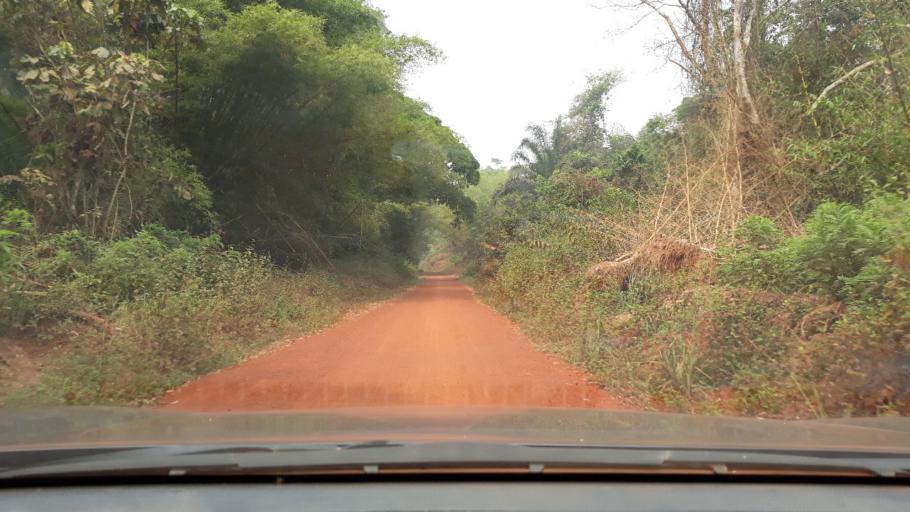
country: CD
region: Eastern Province
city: Aketi
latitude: 2.9169
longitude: 24.0603
